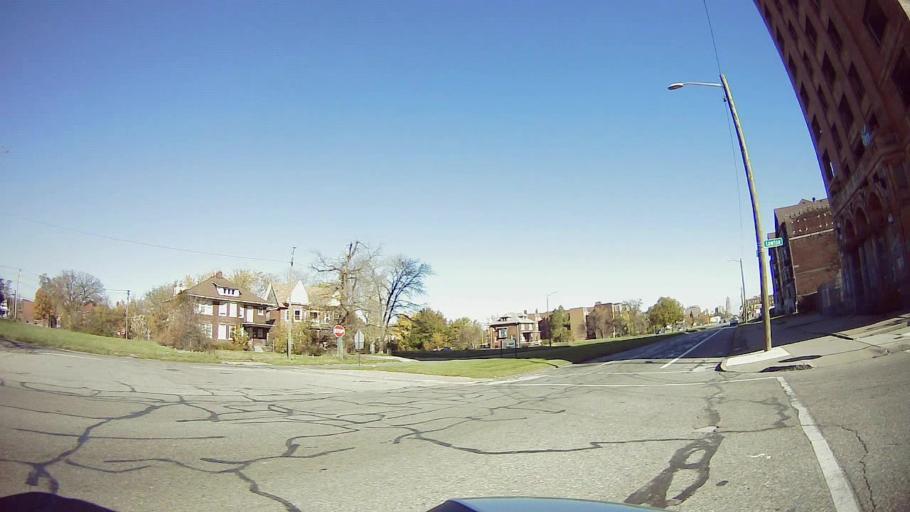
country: US
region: Michigan
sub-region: Wayne County
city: Highland Park
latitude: 42.3589
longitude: -83.1020
